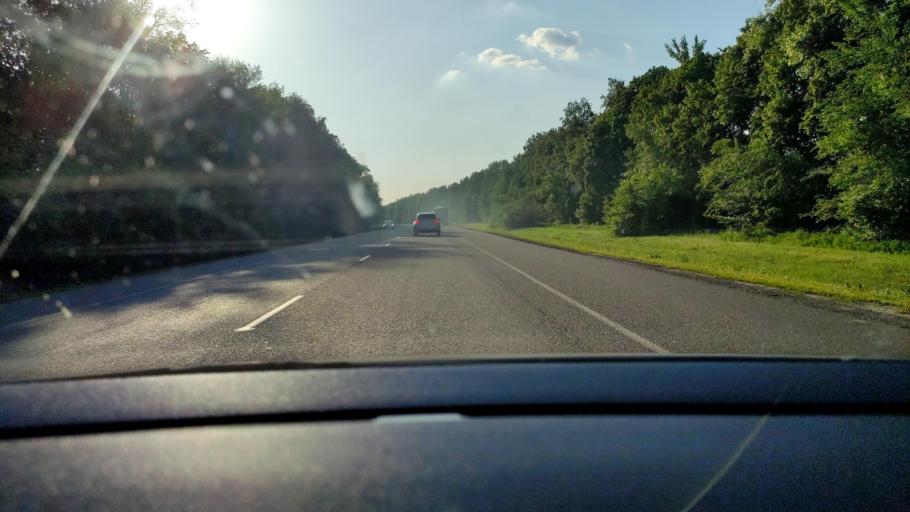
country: RU
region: Voronezj
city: Kashirskoye
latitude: 51.4852
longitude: 39.6519
